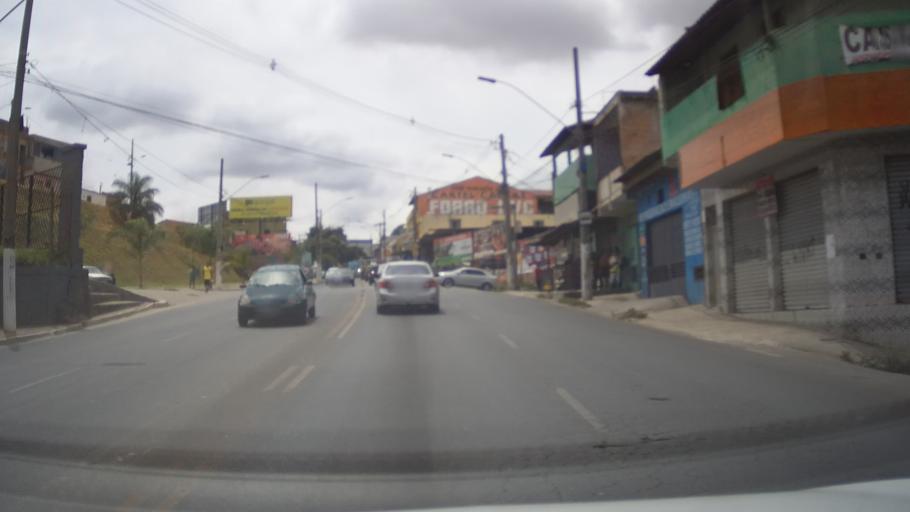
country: BR
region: Minas Gerais
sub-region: Ribeirao Das Neves
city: Ribeirao das Neves
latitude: -19.8025
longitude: -44.0047
